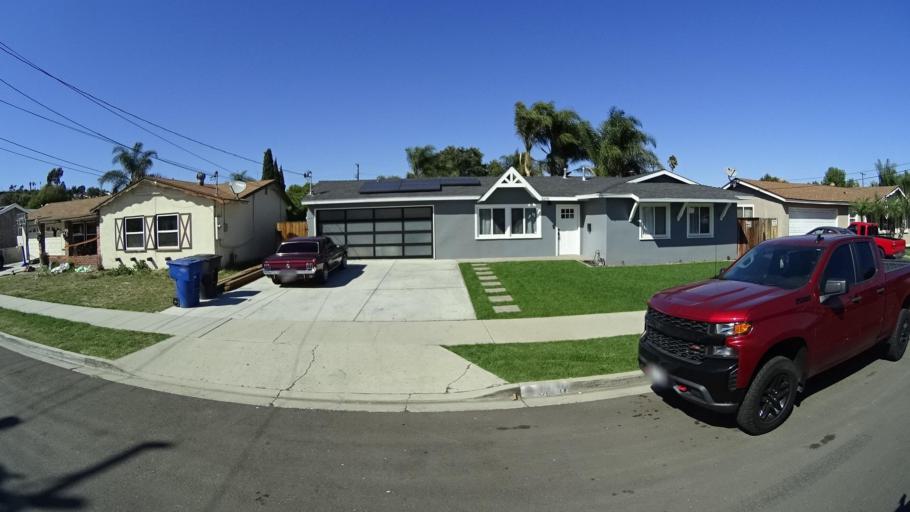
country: US
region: California
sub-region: San Diego County
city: La Presa
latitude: 32.7083
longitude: -117.0158
